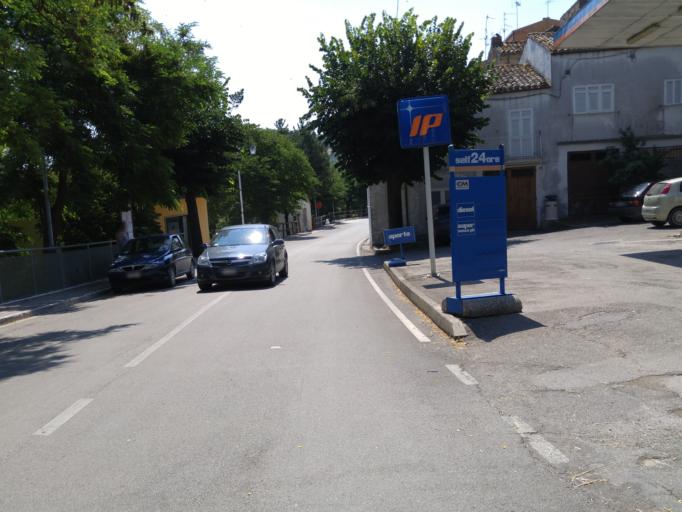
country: IT
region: Abruzzo
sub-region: Provincia di Teramo
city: Castilenti
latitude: 42.5338
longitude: 13.9176
